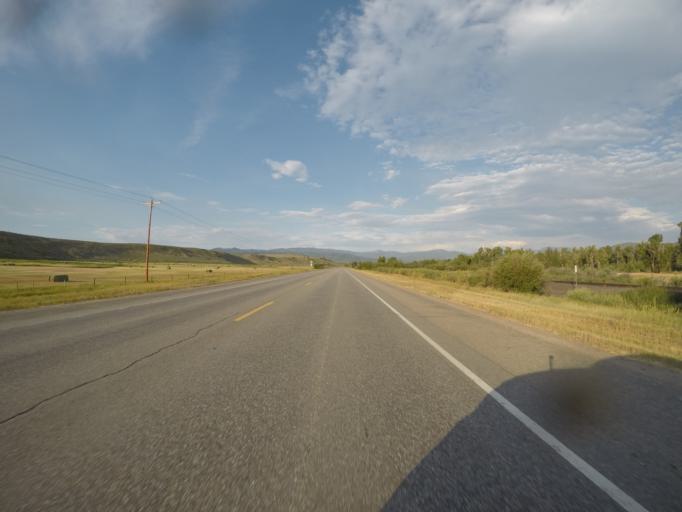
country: US
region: Colorado
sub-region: Routt County
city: Steamboat Springs
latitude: 40.4938
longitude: -106.9494
